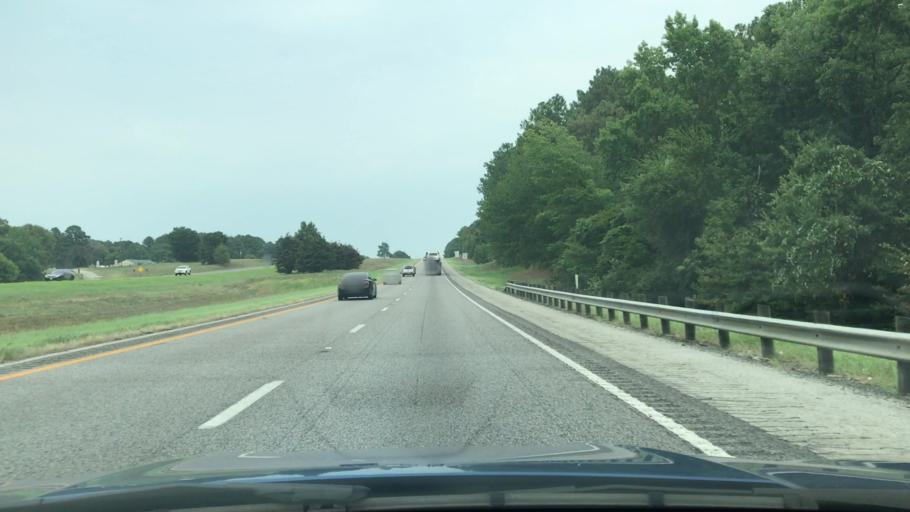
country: US
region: Texas
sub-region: Smith County
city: Lindale
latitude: 32.4683
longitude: -95.3594
